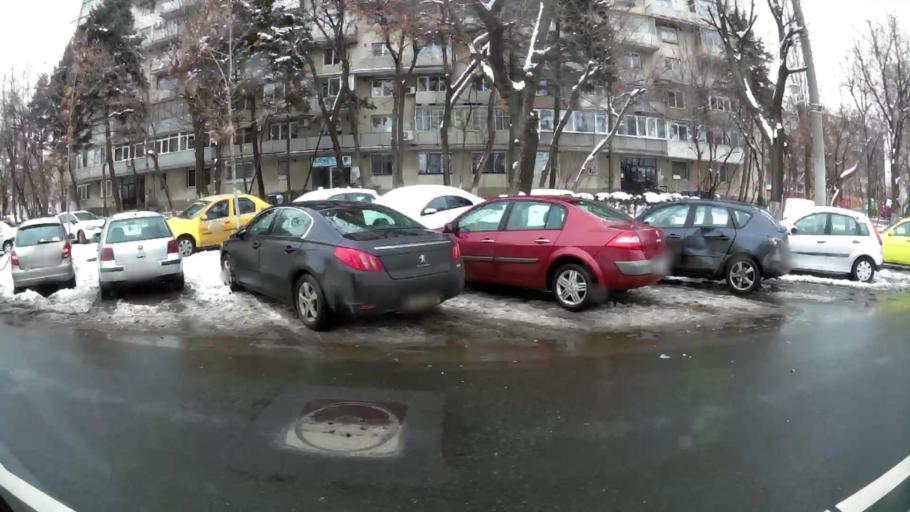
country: RO
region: Bucuresti
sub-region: Municipiul Bucuresti
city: Bucuresti
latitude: 44.3892
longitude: 26.1100
